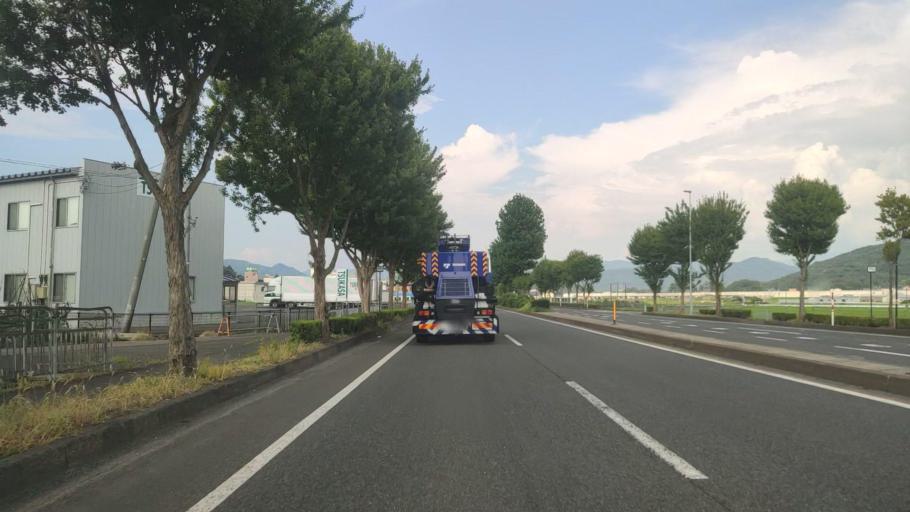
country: JP
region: Fukui
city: Takefu
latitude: 35.8851
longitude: 136.1844
